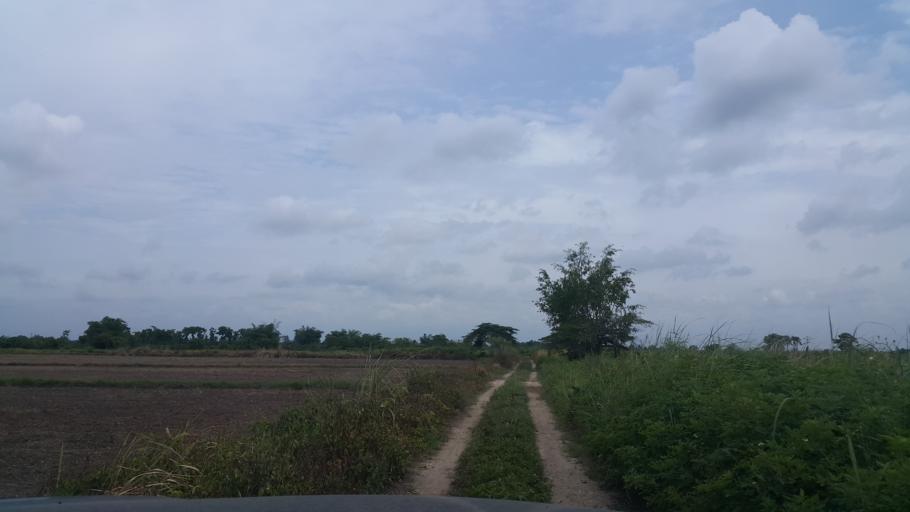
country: TH
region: Lamphun
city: Ban Thi
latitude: 18.6355
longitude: 99.1549
